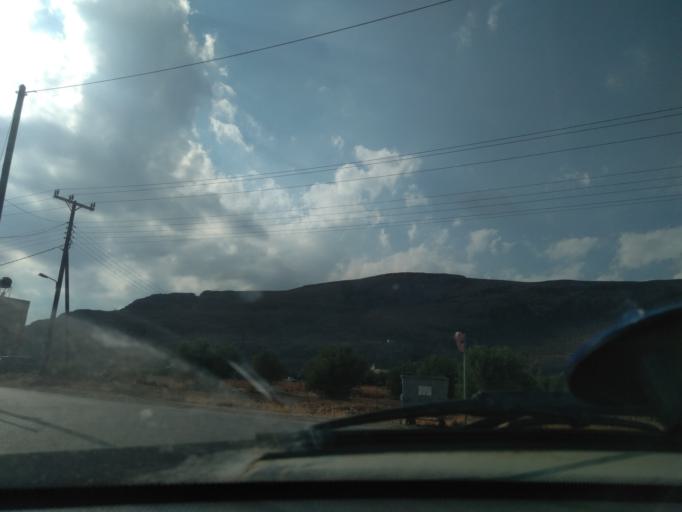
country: GR
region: Crete
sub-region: Nomos Lasithiou
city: Makry-Gialos
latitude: 35.0192
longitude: 26.0314
